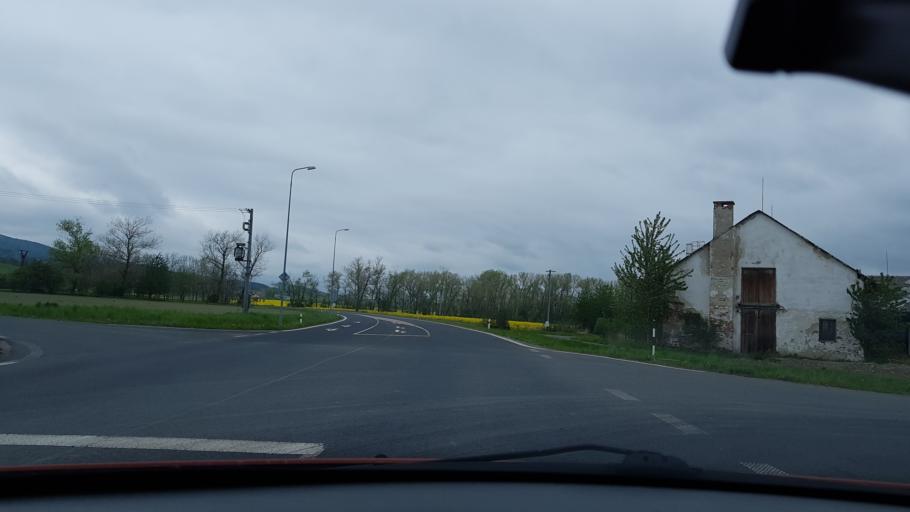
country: CZ
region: Olomoucky
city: Javornik
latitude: 50.3965
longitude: 17.0114
